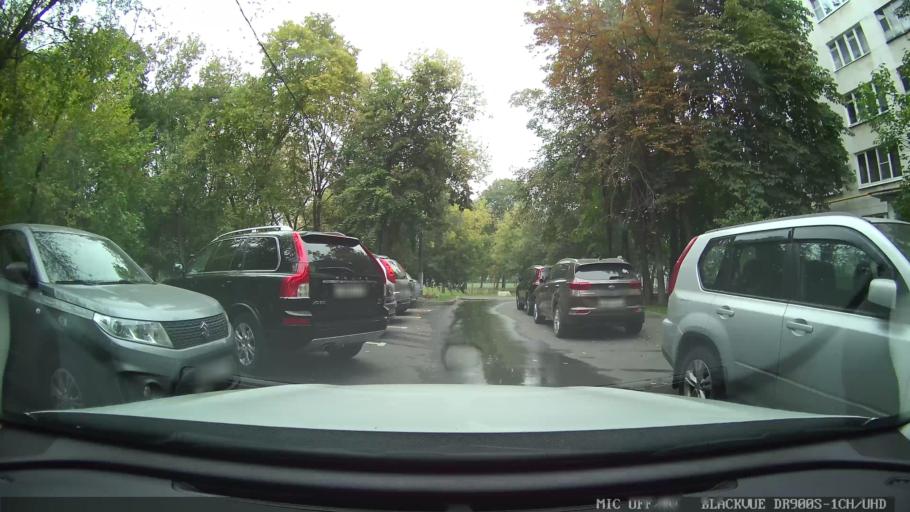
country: RU
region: Moscow
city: Kolomenskoye
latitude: 55.6863
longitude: 37.6870
